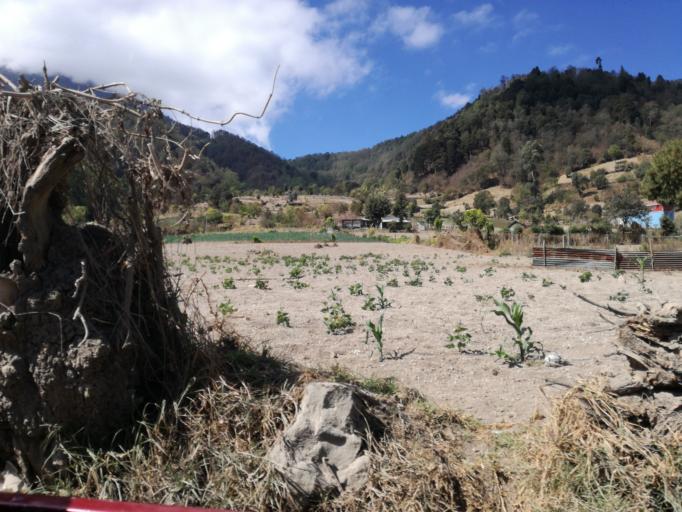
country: GT
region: Quetzaltenango
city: Almolonga
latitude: 14.7872
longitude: -91.5468
